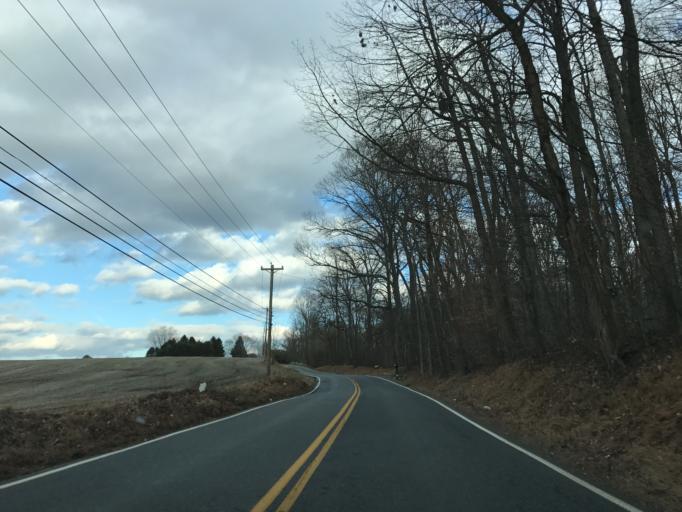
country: US
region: Maryland
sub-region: Cecil County
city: Rising Sun
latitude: 39.6358
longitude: -76.0294
